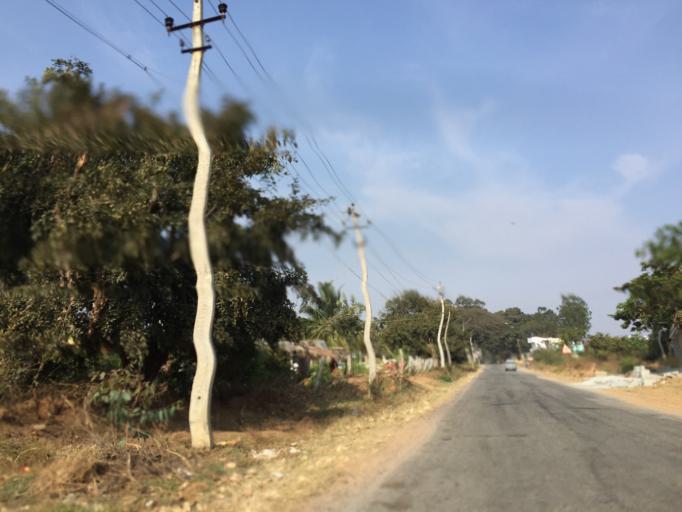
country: IN
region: Karnataka
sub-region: Chikkaballapur
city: Chik Ballapur
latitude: 13.3507
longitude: 77.6594
